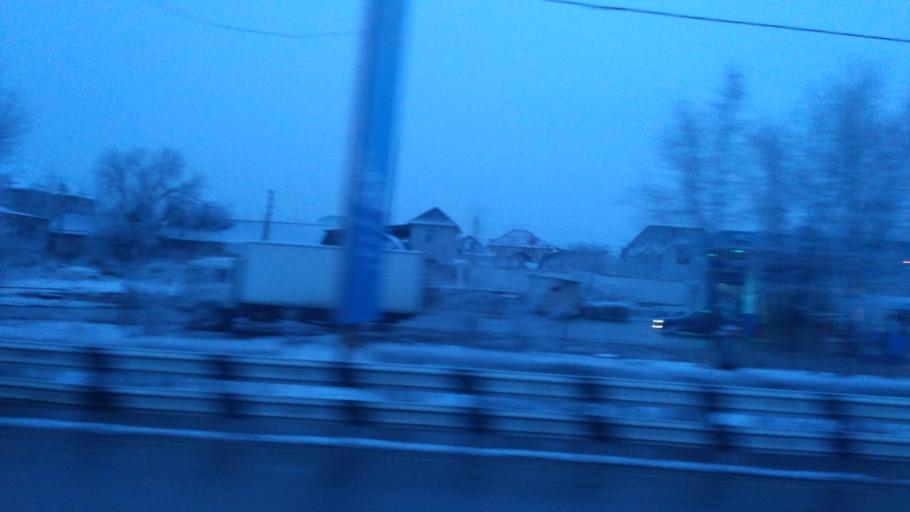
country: KZ
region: Ongtustik Qazaqstan
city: Shymkent
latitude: 42.3582
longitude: 69.5228
